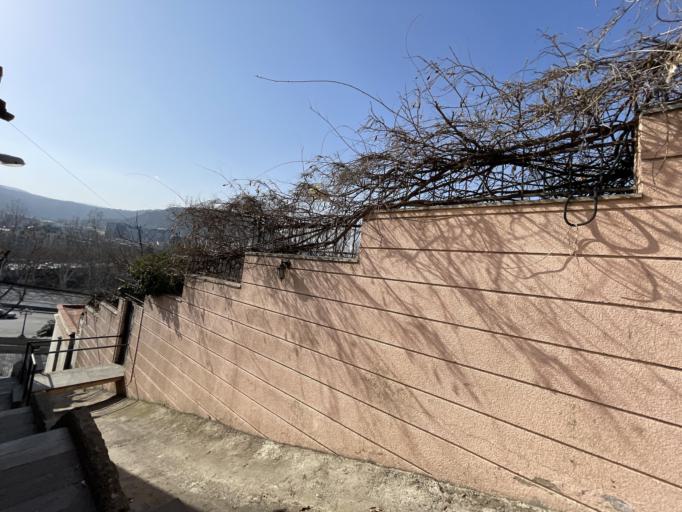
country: GE
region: T'bilisi
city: Tbilisi
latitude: 41.6979
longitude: 44.8103
